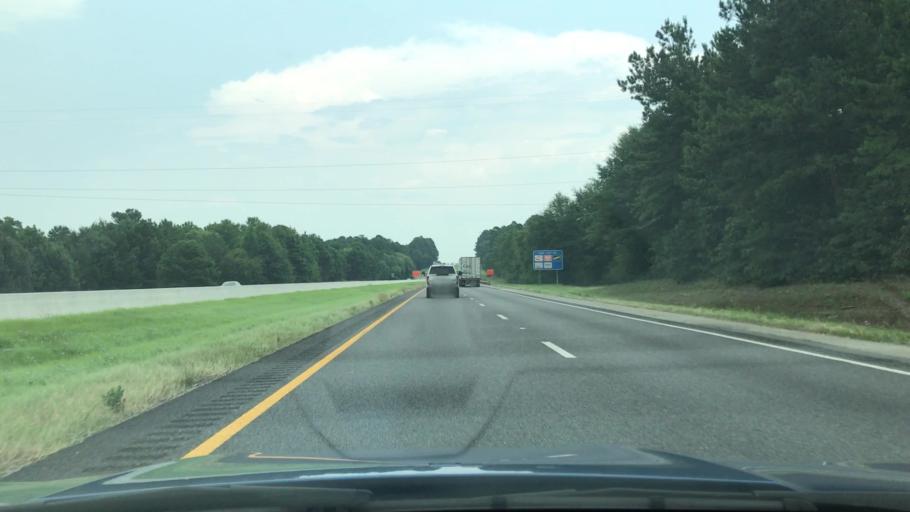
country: US
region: Texas
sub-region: Gregg County
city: Liberty City
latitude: 32.4353
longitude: -94.9612
